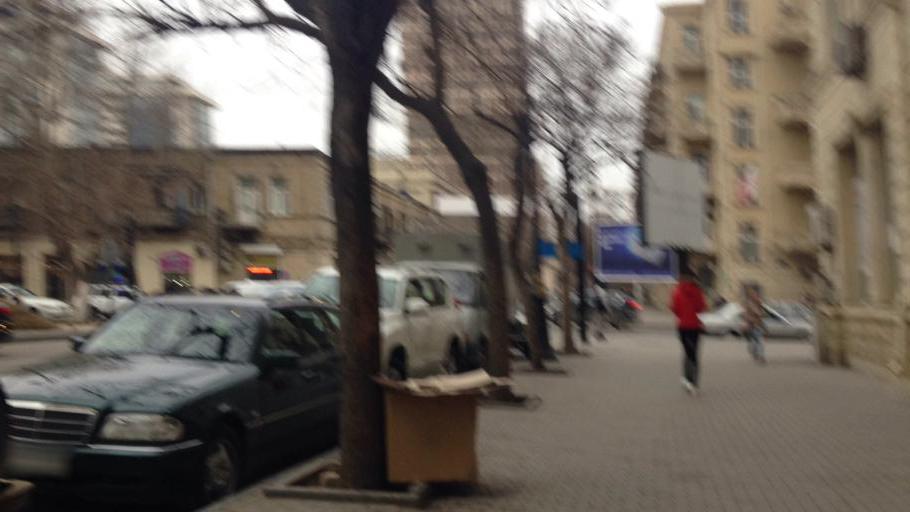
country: AZ
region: Baki
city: Baku
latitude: 40.3770
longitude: 49.8536
